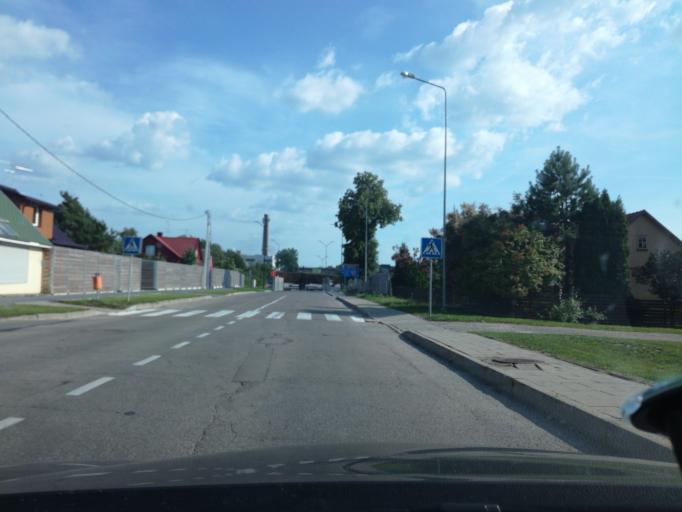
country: LT
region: Marijampoles apskritis
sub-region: Marijampole Municipality
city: Marijampole
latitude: 54.5405
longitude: 23.3499
